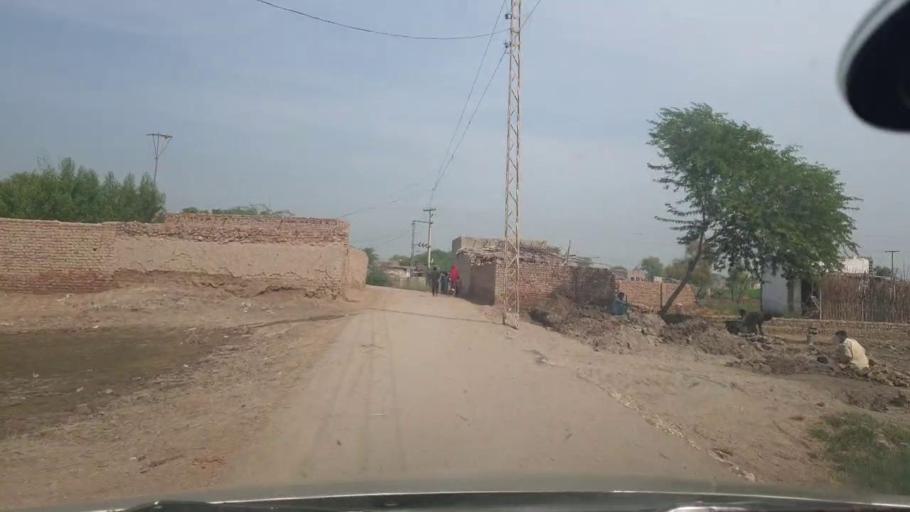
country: PK
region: Sindh
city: Jacobabad
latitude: 28.2958
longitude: 68.4782
